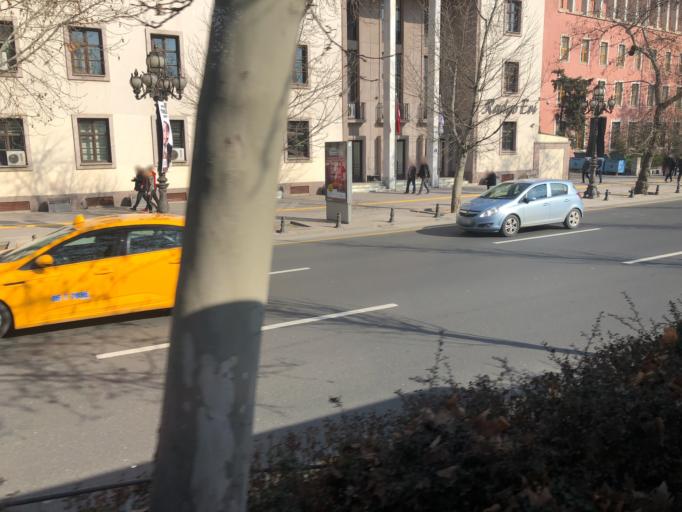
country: TR
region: Ankara
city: Ankara
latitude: 39.9326
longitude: 32.8532
